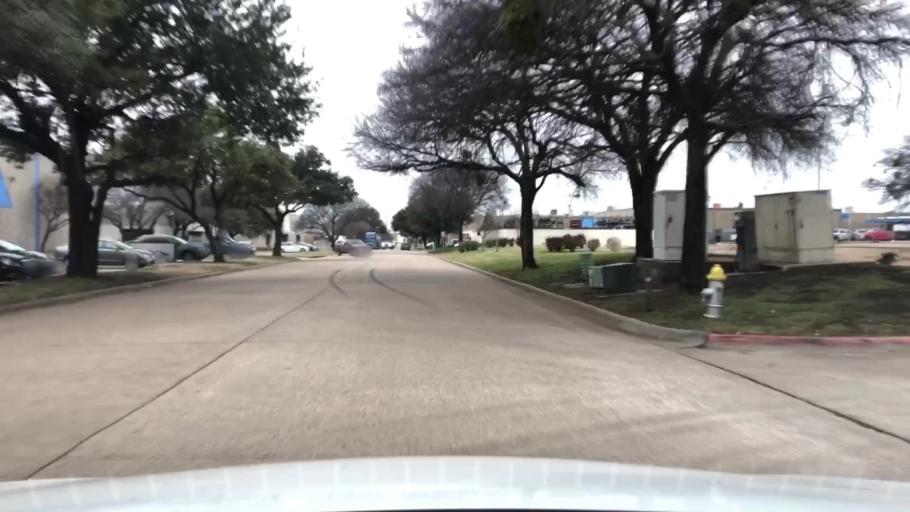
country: US
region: Texas
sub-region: Dallas County
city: Addison
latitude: 32.9605
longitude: -96.8417
